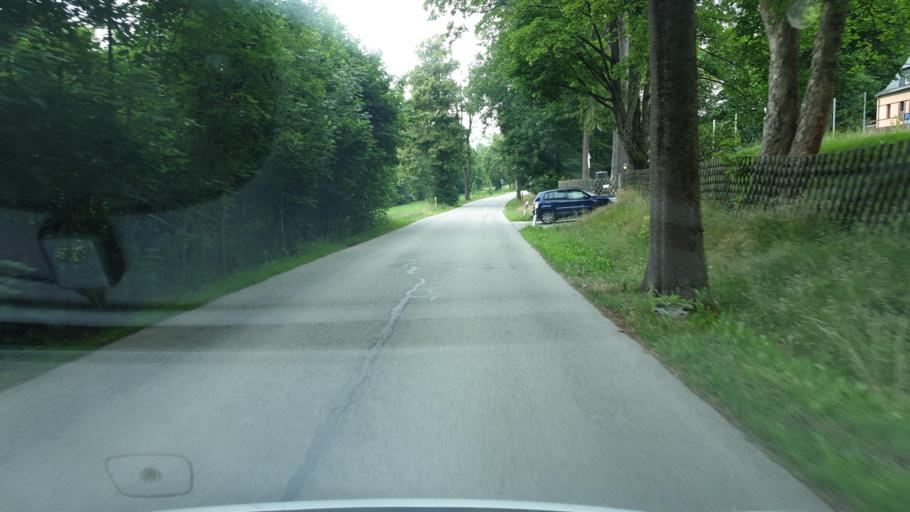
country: DE
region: Saxony
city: Grunhain
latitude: 50.5818
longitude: 12.8262
